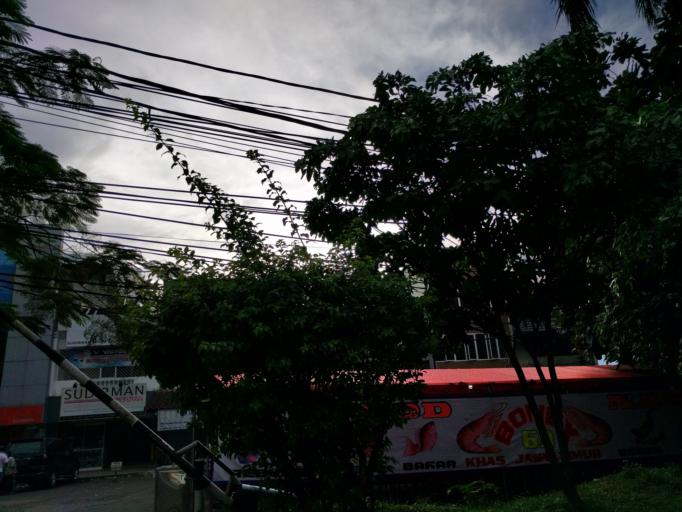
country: ID
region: West Java
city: Bogor
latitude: -6.5874
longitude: 106.7969
